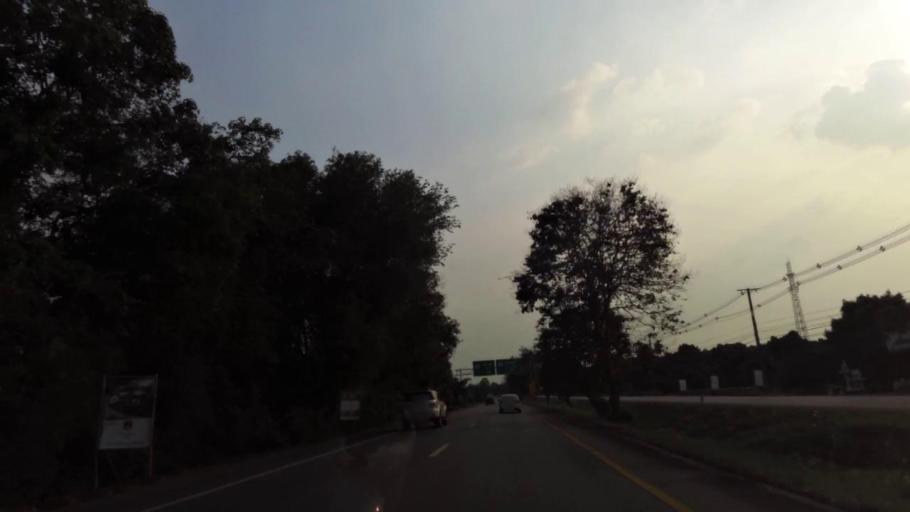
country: TH
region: Chanthaburi
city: Chanthaburi
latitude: 12.5331
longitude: 102.1575
